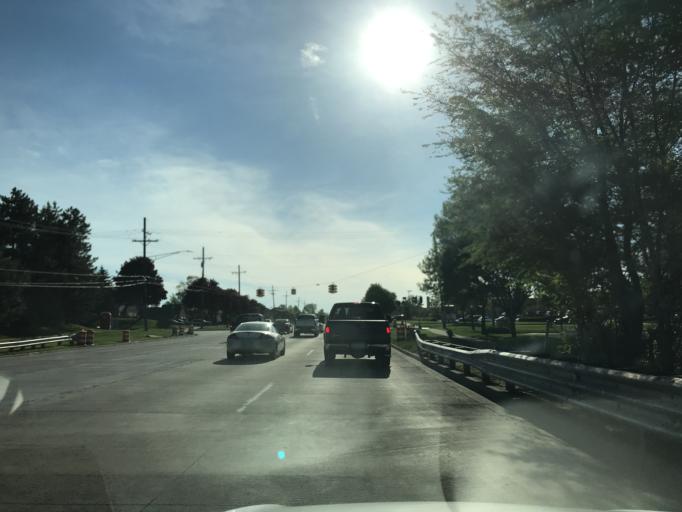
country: US
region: Michigan
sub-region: Oakland County
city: Farmington
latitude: 42.4404
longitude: -83.3841
